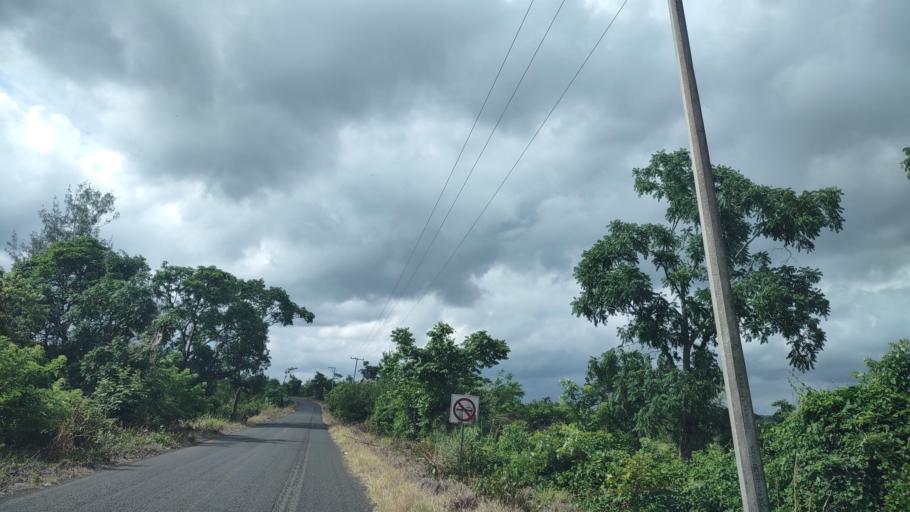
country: MX
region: Veracruz
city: Gutierrez Zamora
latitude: 20.2970
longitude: -97.1354
